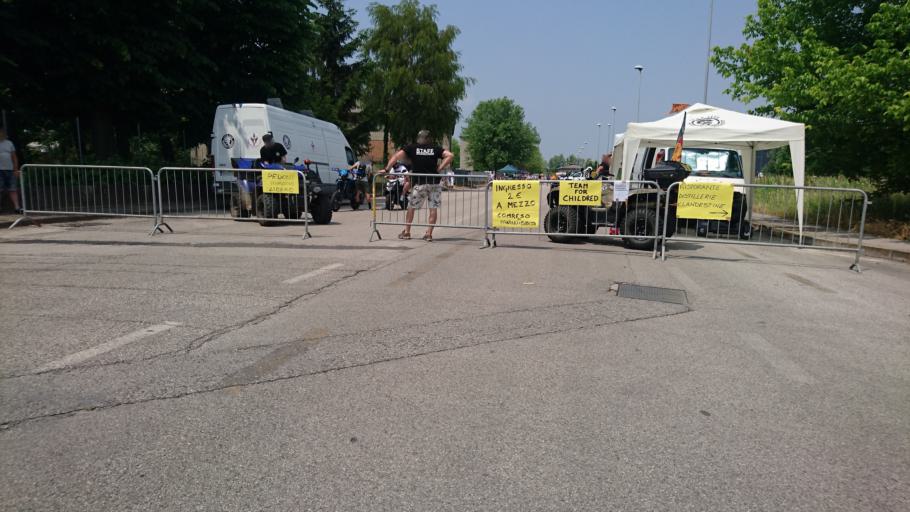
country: IT
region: Veneto
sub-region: Provincia di Padova
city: Cartura
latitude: 45.2817
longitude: 11.8677
